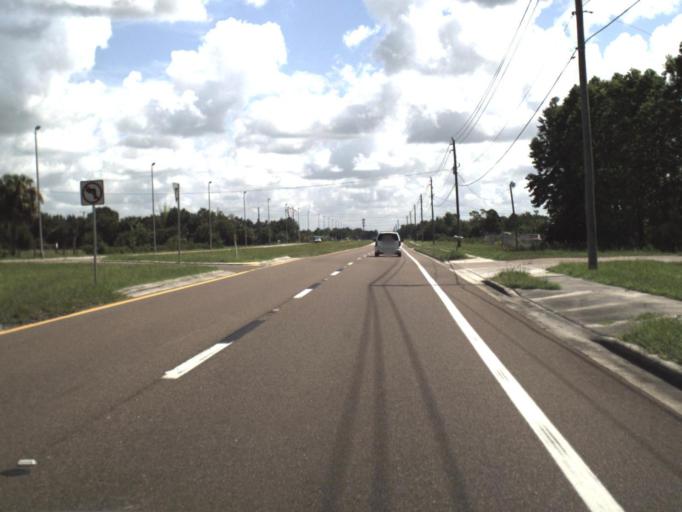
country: US
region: Florida
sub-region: Charlotte County
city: Cleveland
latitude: 26.9650
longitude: -81.9755
